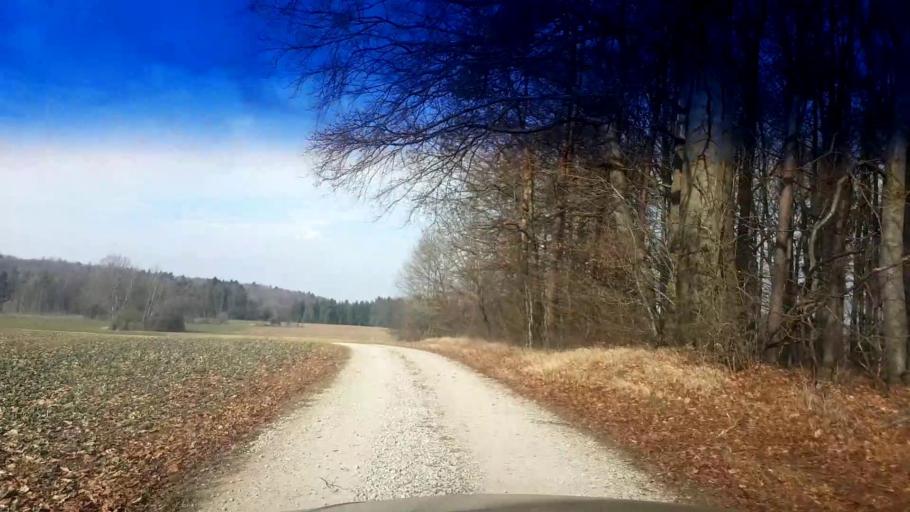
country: DE
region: Bavaria
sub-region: Upper Franconia
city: Poxdorf
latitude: 49.9287
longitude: 11.0664
